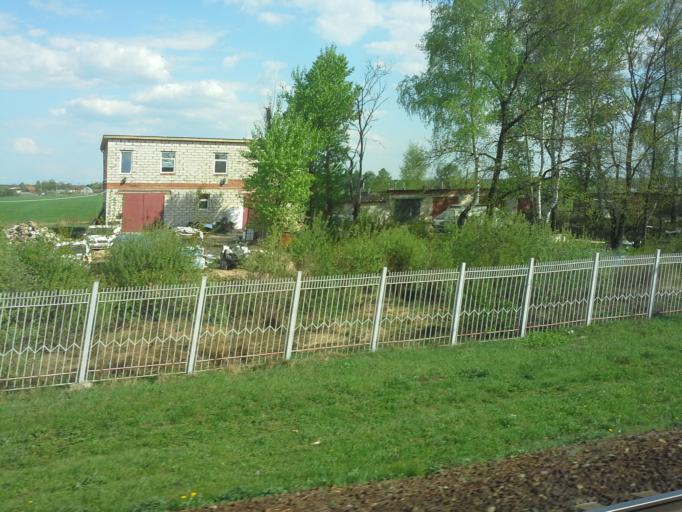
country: RU
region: Moskovskaya
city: Pravdinskiy
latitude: 56.0515
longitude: 37.8606
